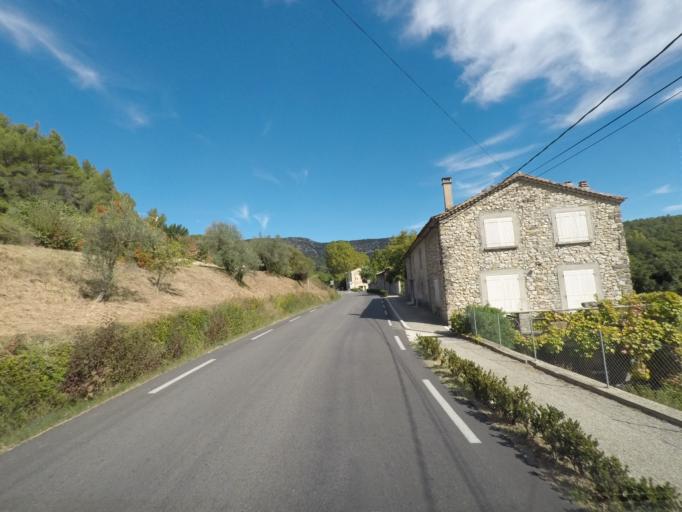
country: FR
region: Rhone-Alpes
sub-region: Departement de la Drome
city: Nyons
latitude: 44.3753
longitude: 5.1667
